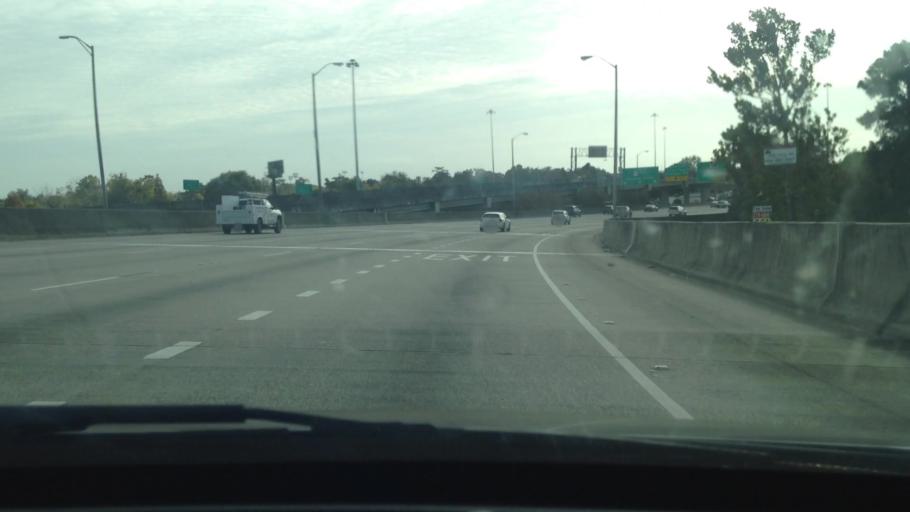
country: US
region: Louisiana
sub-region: Jefferson Parish
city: Gretna
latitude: 29.9372
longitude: -90.0402
